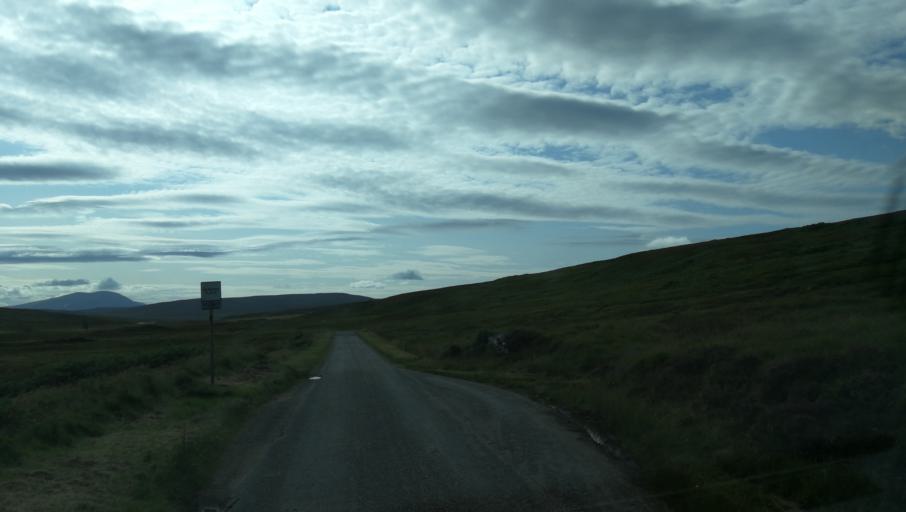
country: GB
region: Scotland
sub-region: Highland
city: Golspie
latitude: 58.3662
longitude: -4.3944
